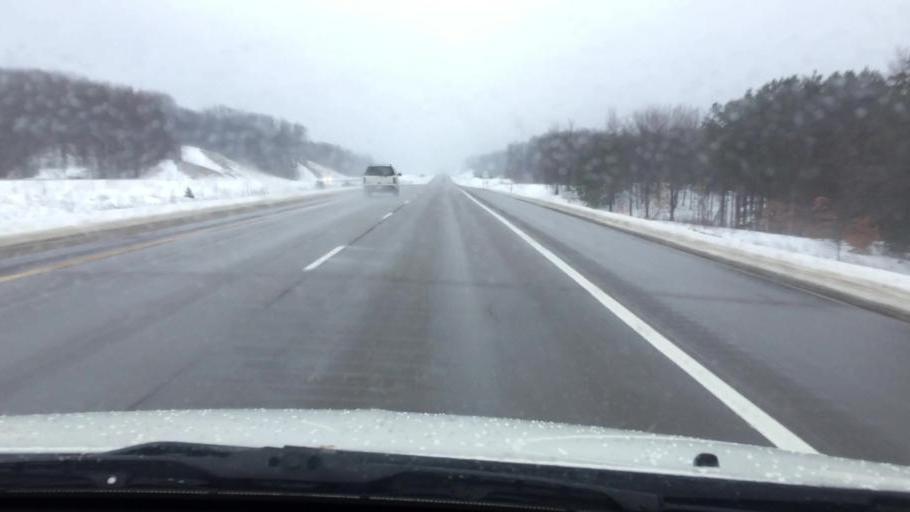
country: US
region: Michigan
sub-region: Wexford County
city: Manton
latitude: 44.3619
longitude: -85.4029
